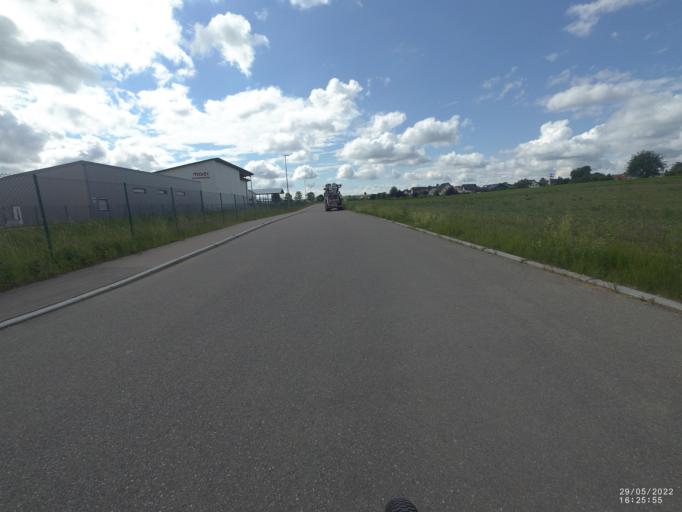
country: DE
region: Baden-Wuerttemberg
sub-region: Regierungsbezirk Stuttgart
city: Bolheim
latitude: 48.5926
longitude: 10.1213
